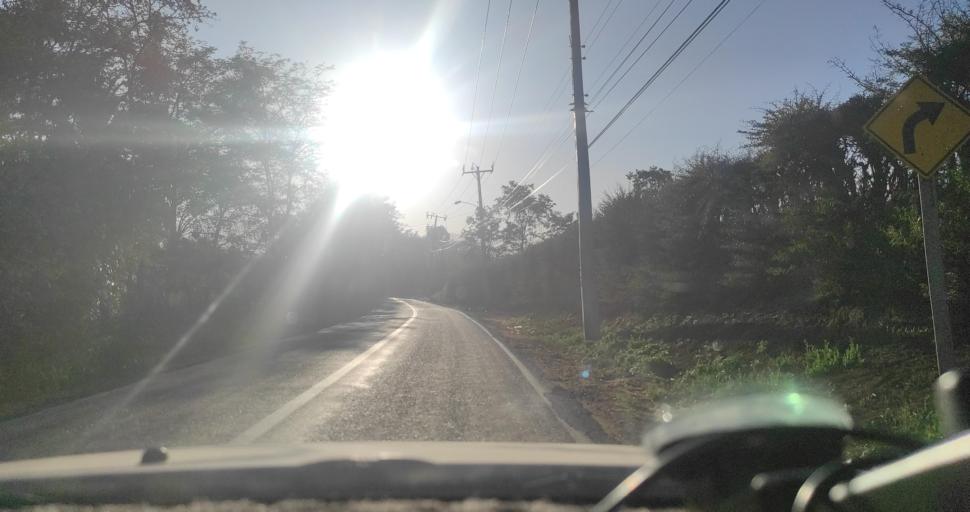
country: CL
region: Valparaiso
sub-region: Provincia de Marga Marga
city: Limache
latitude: -33.0048
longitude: -71.2285
